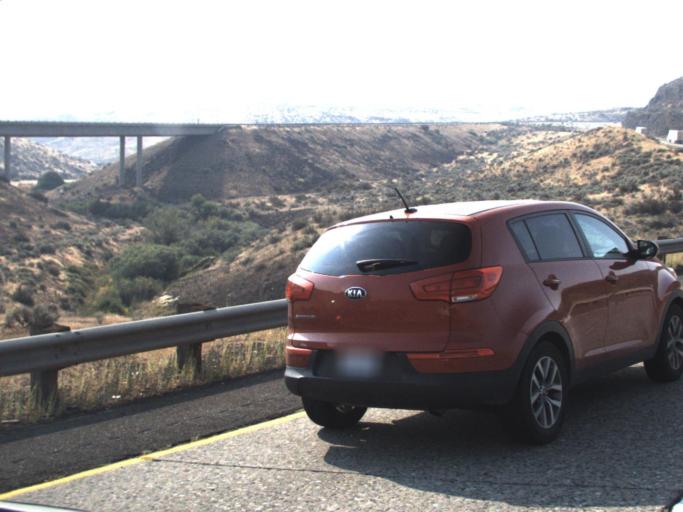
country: US
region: Washington
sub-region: Kittitas County
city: Kittitas
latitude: 46.8014
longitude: -120.3618
